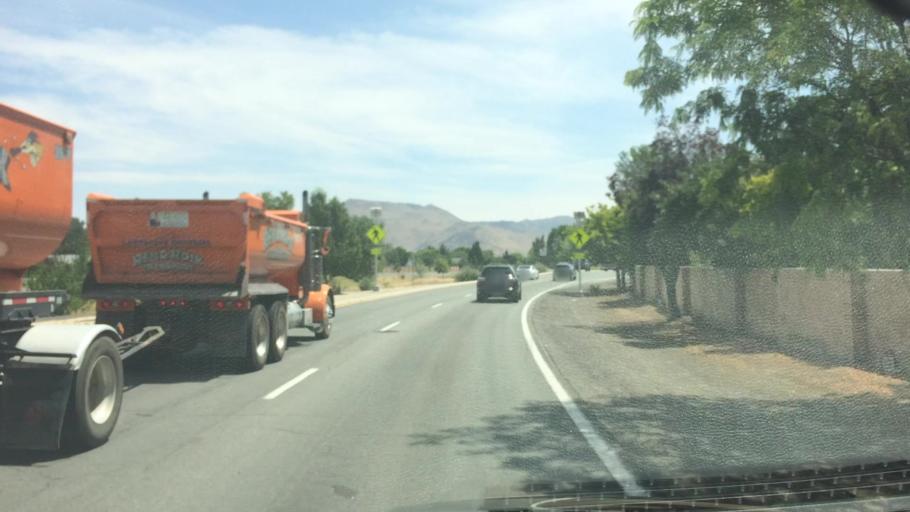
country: US
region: Nevada
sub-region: Washoe County
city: Sparks
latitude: 39.5483
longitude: -119.7156
